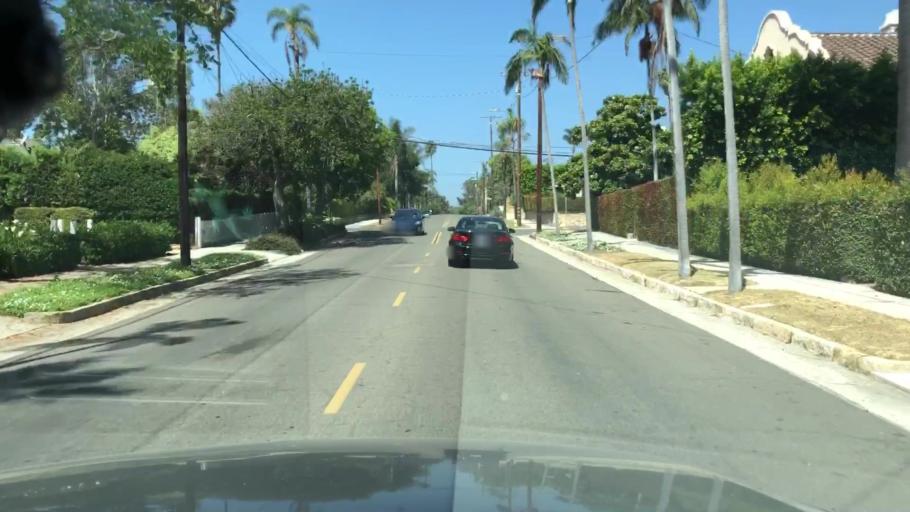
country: US
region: California
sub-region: Santa Barbara County
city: Mission Canyon
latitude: 34.4346
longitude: -119.7121
